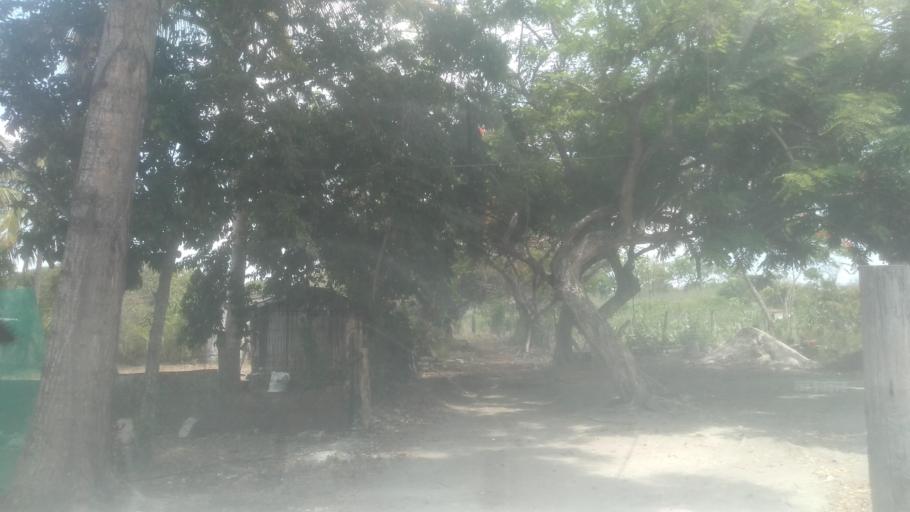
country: MX
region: Veracruz
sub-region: Emiliano Zapata
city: Plan del Rio
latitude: 19.4300
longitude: -96.6990
